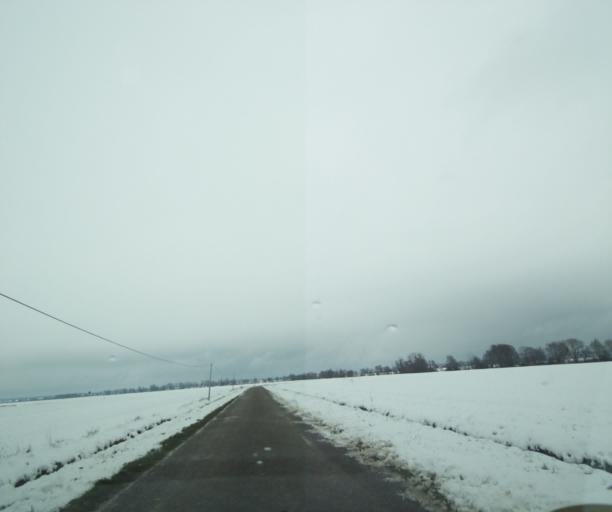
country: FR
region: Champagne-Ardenne
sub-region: Departement de la Haute-Marne
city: Montier-en-Der
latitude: 48.4291
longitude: 4.7892
